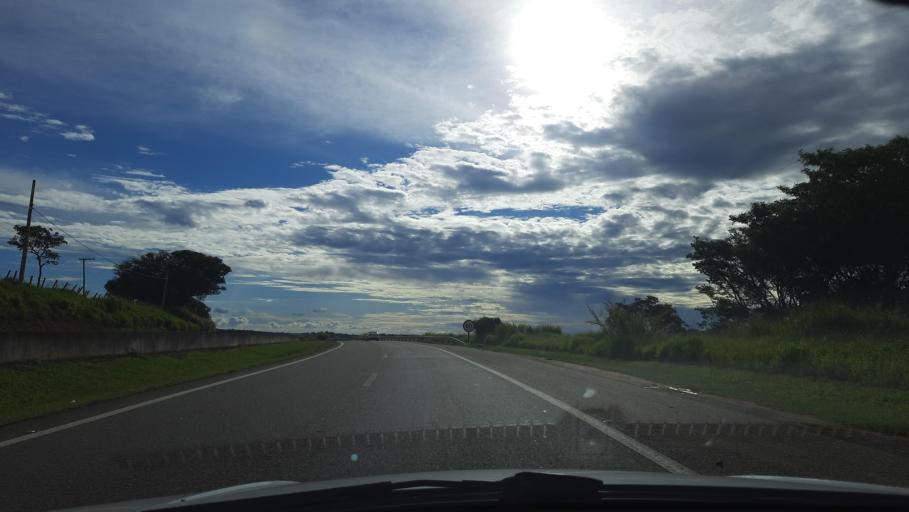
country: BR
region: Sao Paulo
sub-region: Sao Joao Da Boa Vista
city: Sao Joao da Boa Vista
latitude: -21.9528
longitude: -46.7280
